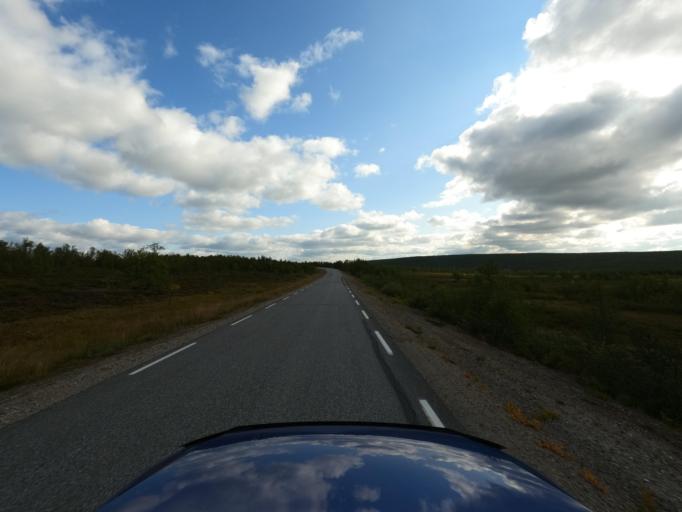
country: NO
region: Finnmark Fylke
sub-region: Porsanger
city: Lakselv
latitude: 69.3737
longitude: 24.4112
